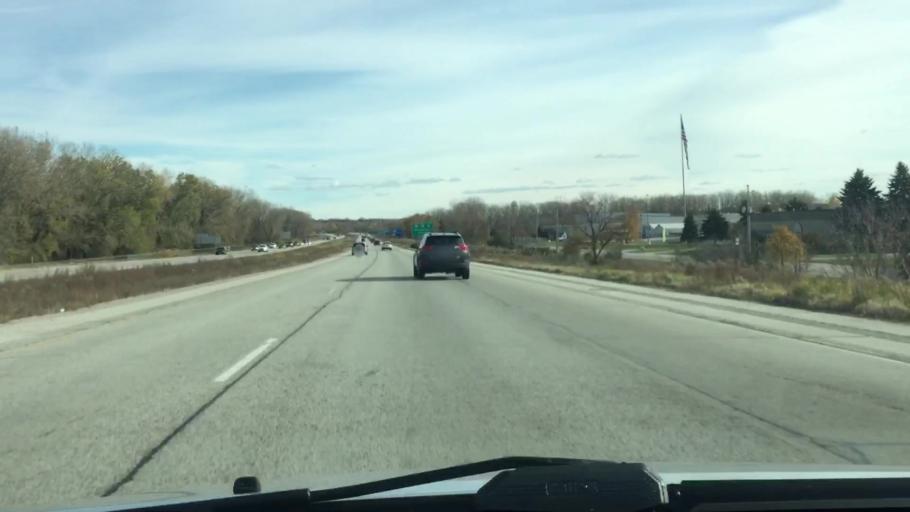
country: US
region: Wisconsin
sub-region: Brown County
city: Green Bay
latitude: 44.5250
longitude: -87.9834
